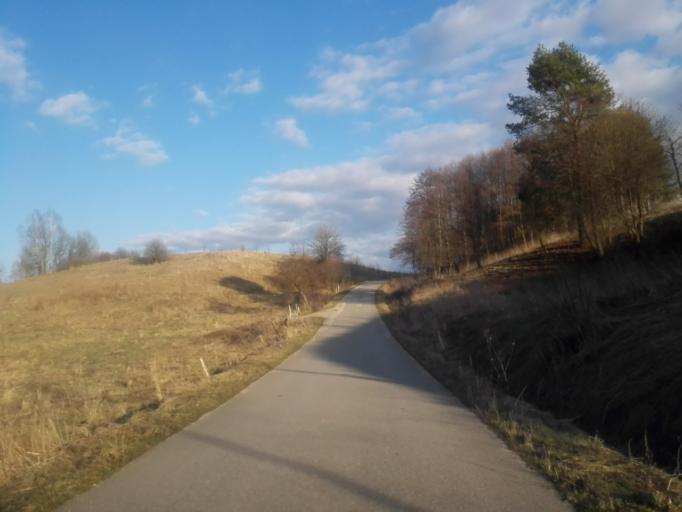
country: PL
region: Podlasie
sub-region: Suwalki
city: Suwalki
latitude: 54.2150
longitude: 23.0009
